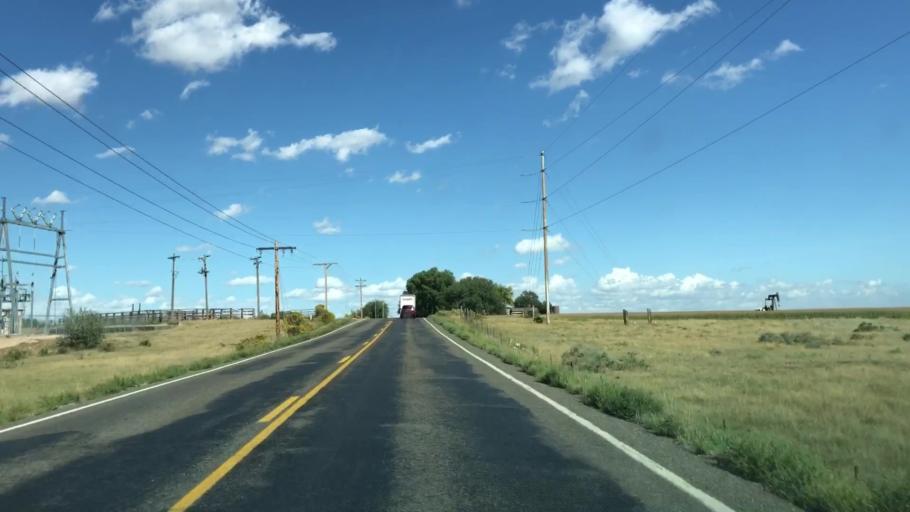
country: US
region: Colorado
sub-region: Larimer County
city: Wellington
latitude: 40.7547
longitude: -105.0492
